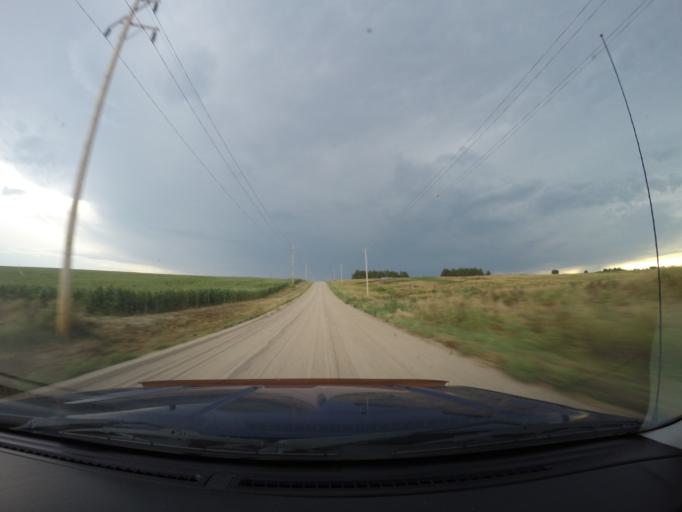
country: US
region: Nebraska
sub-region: Buffalo County
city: Kearney
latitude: 40.8442
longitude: -99.2073
